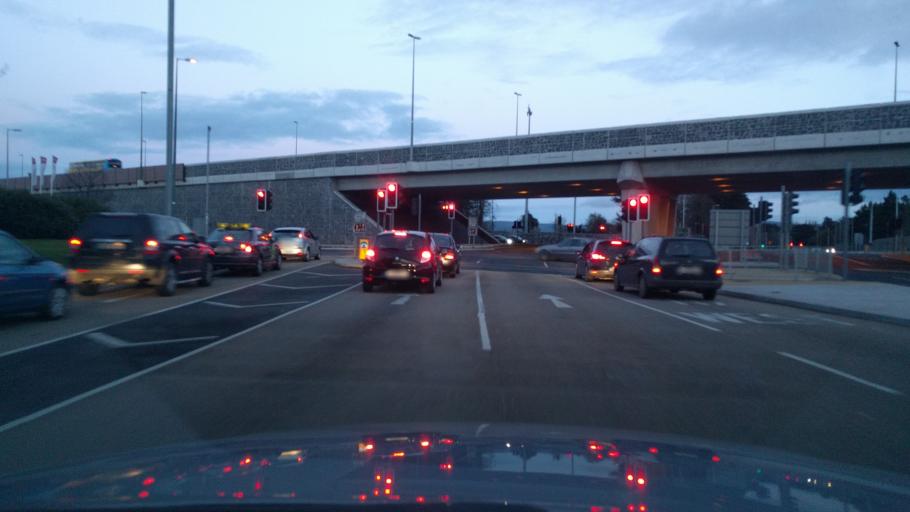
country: IE
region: Leinster
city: Clondalkin
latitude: 53.3134
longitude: -6.3912
